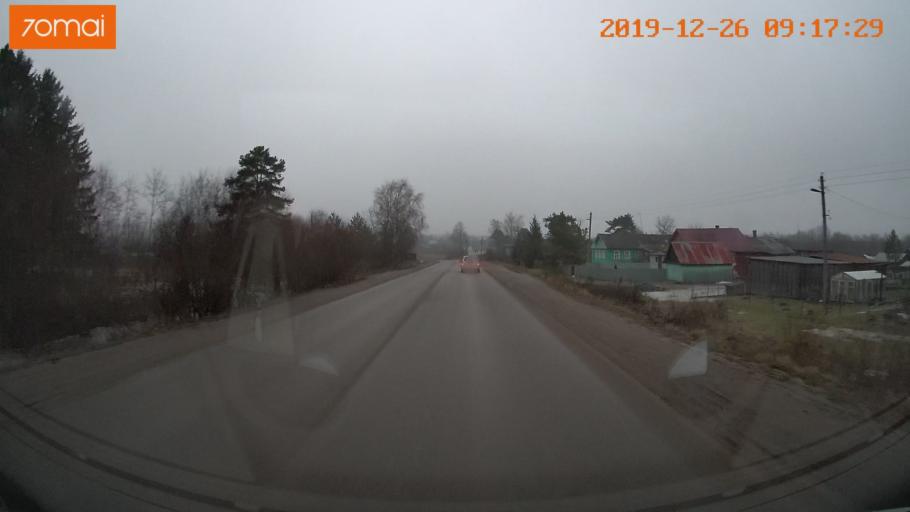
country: RU
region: Vologda
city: Gryazovets
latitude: 58.9302
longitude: 40.2397
